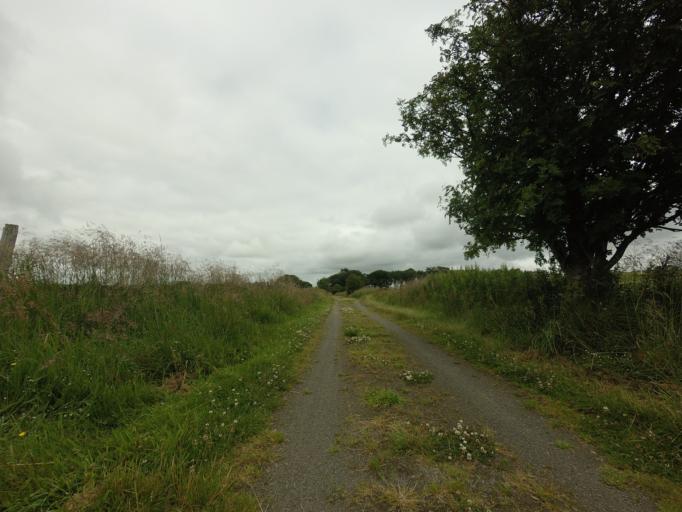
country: GB
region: Scotland
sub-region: Aberdeenshire
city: Mintlaw
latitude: 57.4895
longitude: -2.1347
